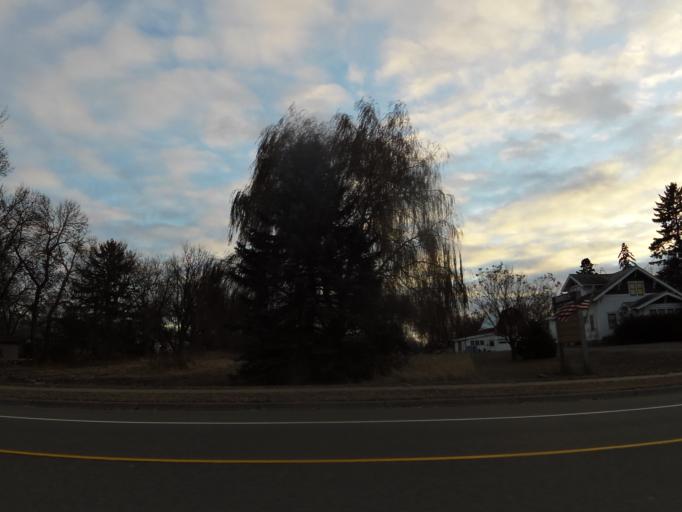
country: US
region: Minnesota
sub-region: Ramsey County
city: White Bear Lake
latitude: 45.0503
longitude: -93.0240
